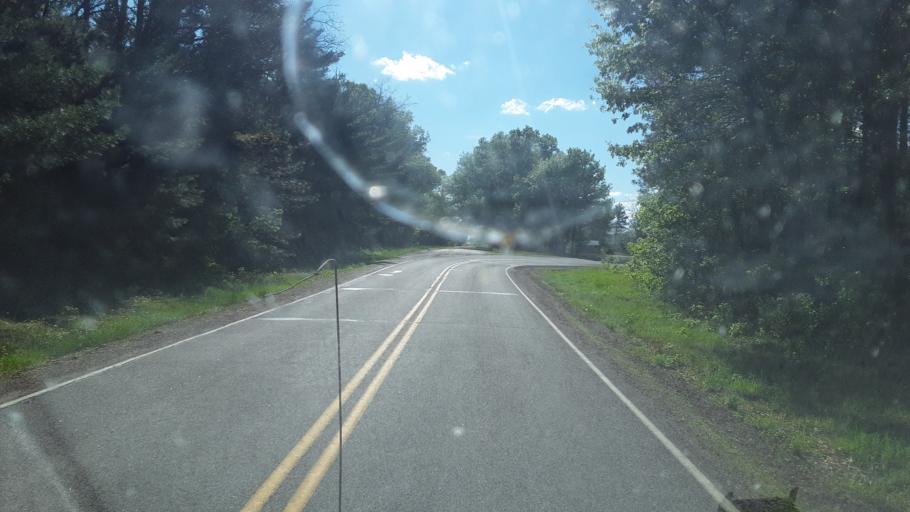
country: US
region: Wisconsin
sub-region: Wood County
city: Nekoosa
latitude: 44.3069
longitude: -90.1284
